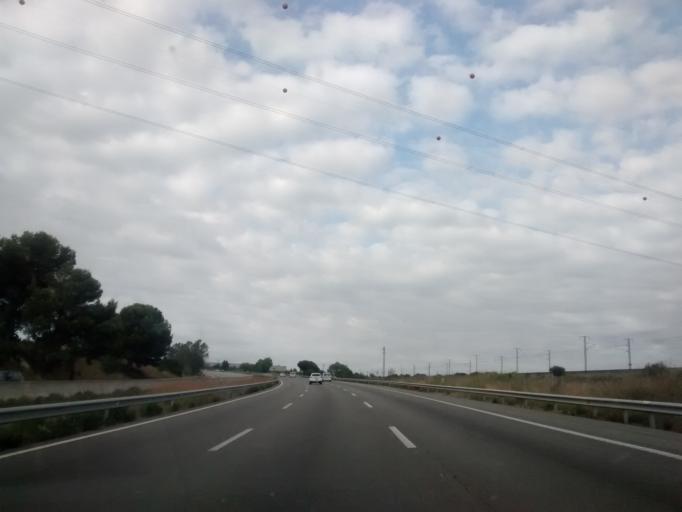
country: ES
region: Catalonia
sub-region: Provincia de Barcelona
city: La Granada
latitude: 41.3836
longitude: 1.7405
